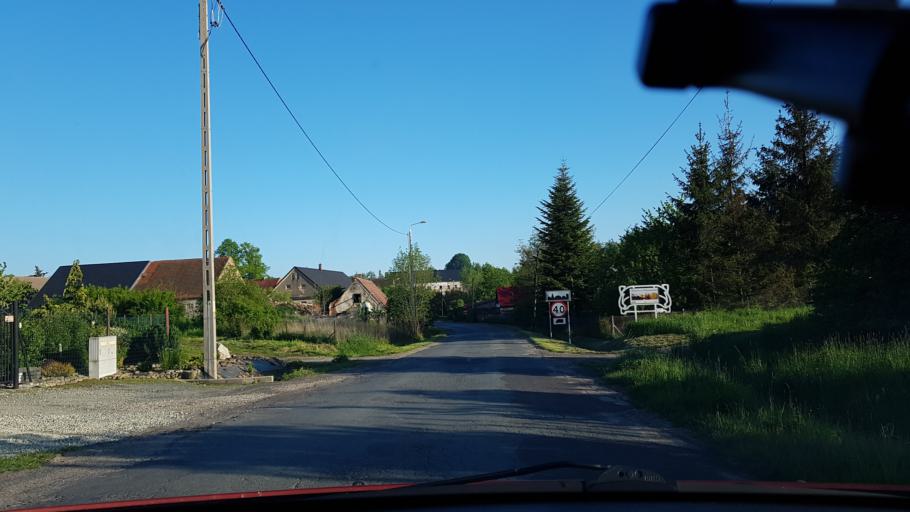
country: PL
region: Lower Silesian Voivodeship
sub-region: Powiat zabkowicki
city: Stoszowice
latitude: 50.6017
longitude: 16.7376
